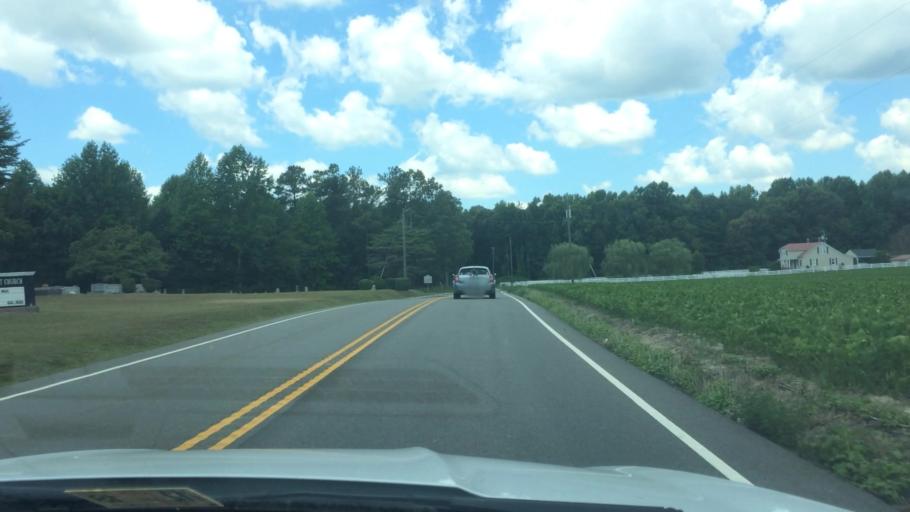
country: US
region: Virginia
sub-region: King William County
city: West Point
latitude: 37.6029
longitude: -76.7702
